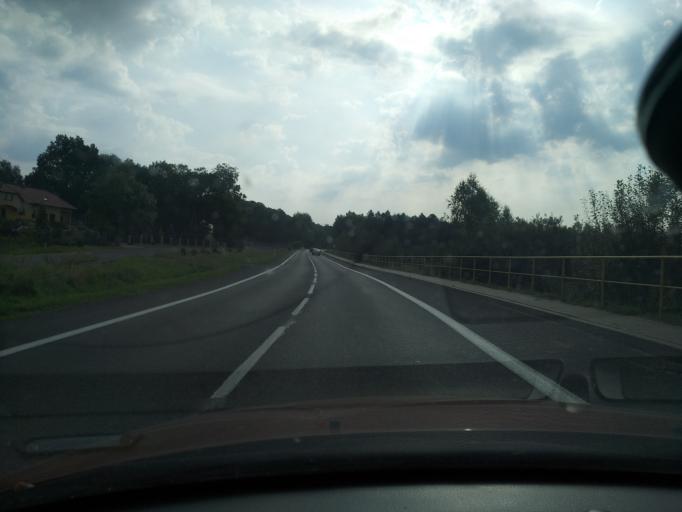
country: PL
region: Lower Silesian Voivodeship
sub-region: Powiat lubanski
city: Olszyna
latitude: 51.0811
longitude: 15.3357
